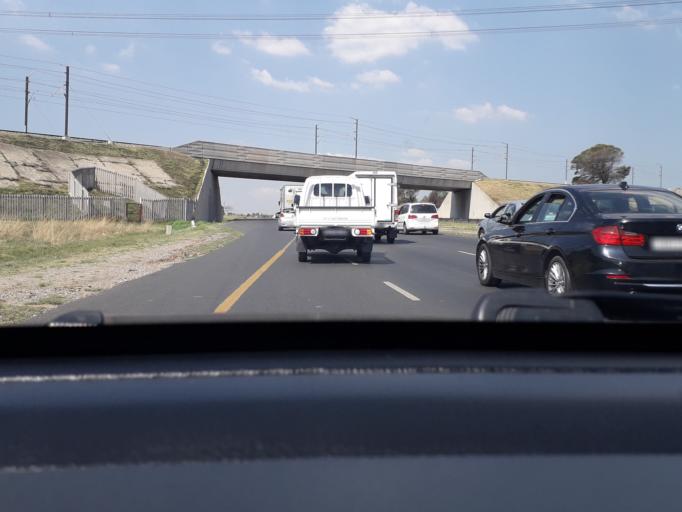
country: ZA
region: Gauteng
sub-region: City of Johannesburg Metropolitan Municipality
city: Modderfontein
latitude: -26.1029
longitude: 28.1773
